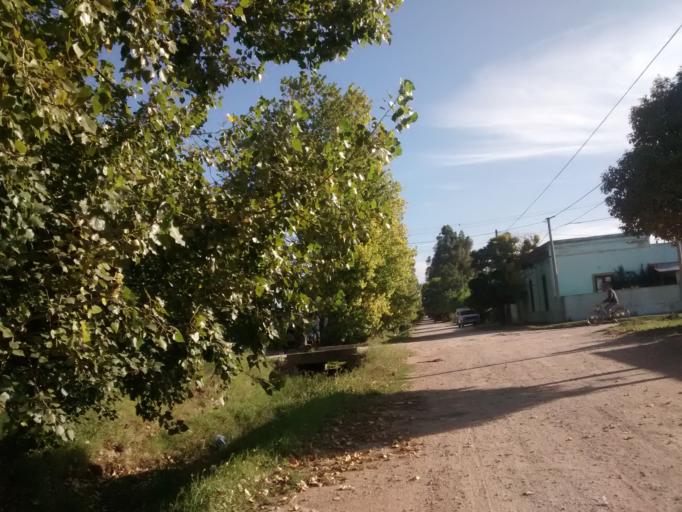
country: AR
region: Buenos Aires
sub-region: Partido de Loberia
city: Loberia
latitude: -38.1707
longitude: -58.7844
